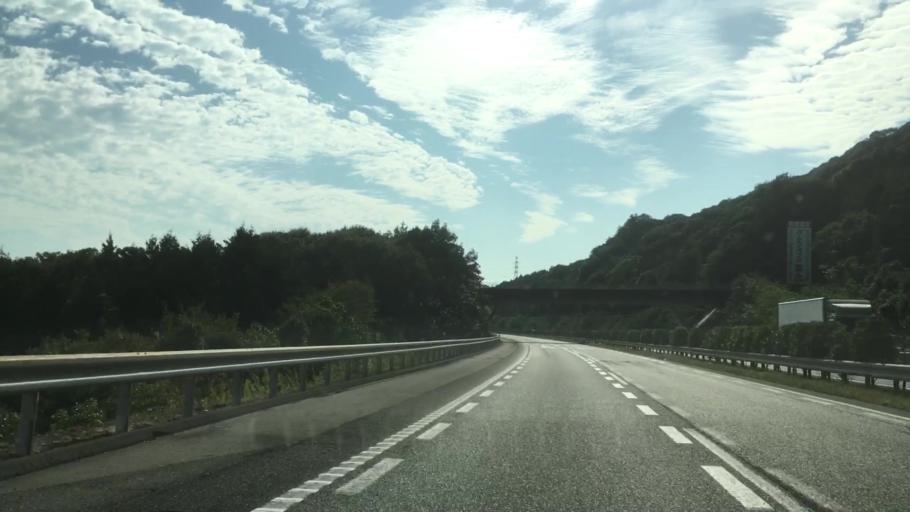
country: JP
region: Yamaguchi
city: Hikari
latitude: 34.0579
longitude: 132.0073
